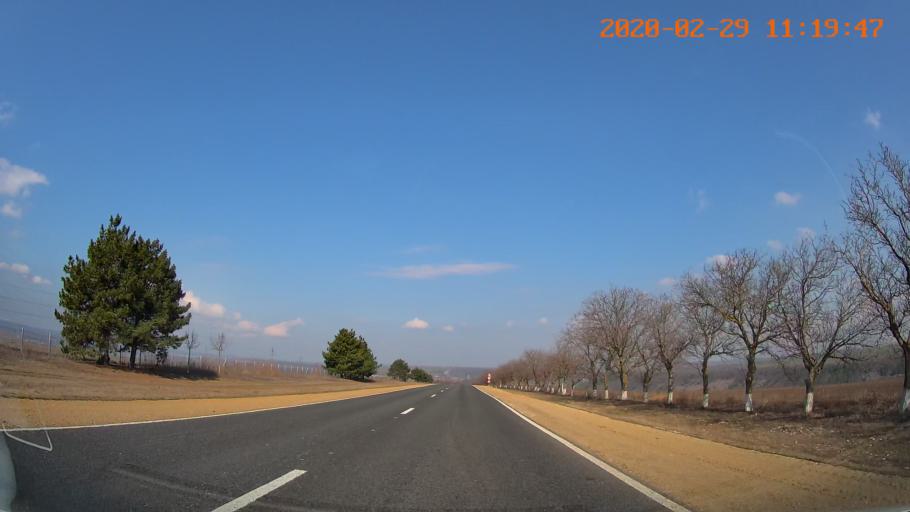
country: MD
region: Telenesti
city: Cocieri
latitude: 47.3554
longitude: 29.1734
